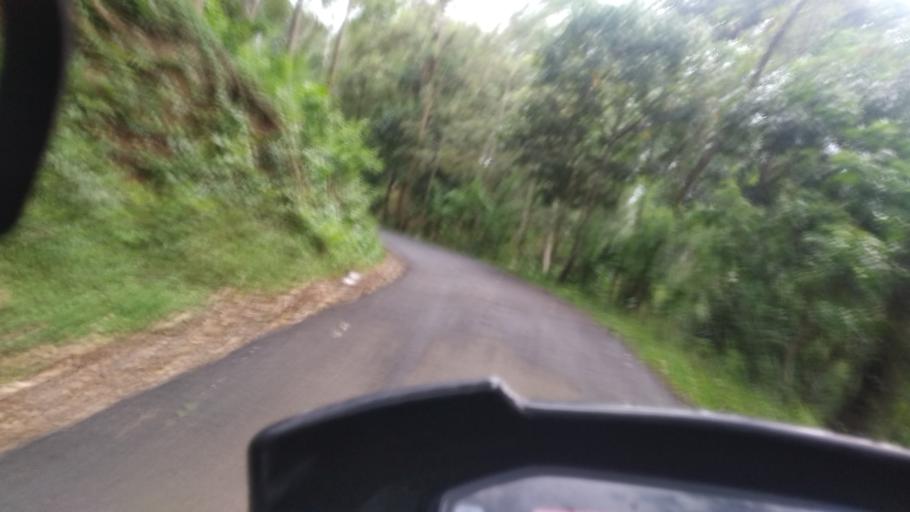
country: IN
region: Tamil Nadu
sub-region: Theni
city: Gudalur
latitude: 9.5545
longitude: 77.0674
